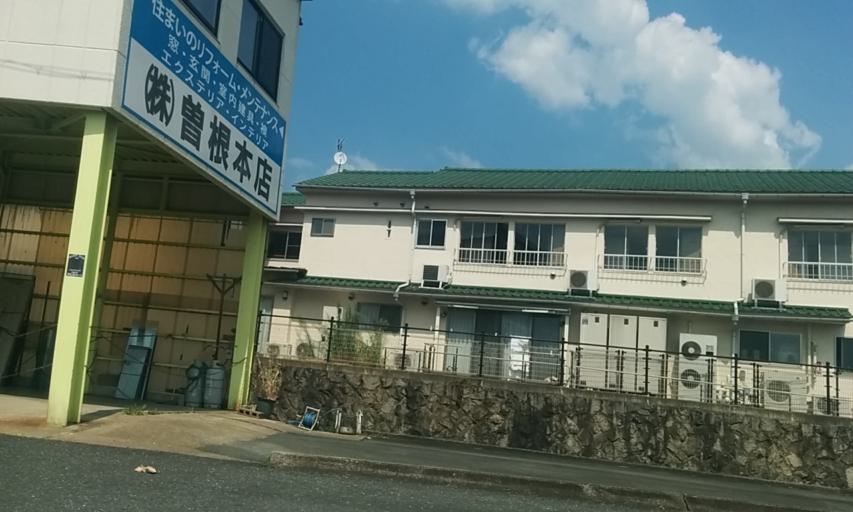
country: JP
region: Kyoto
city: Fukuchiyama
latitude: 35.3065
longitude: 135.1297
